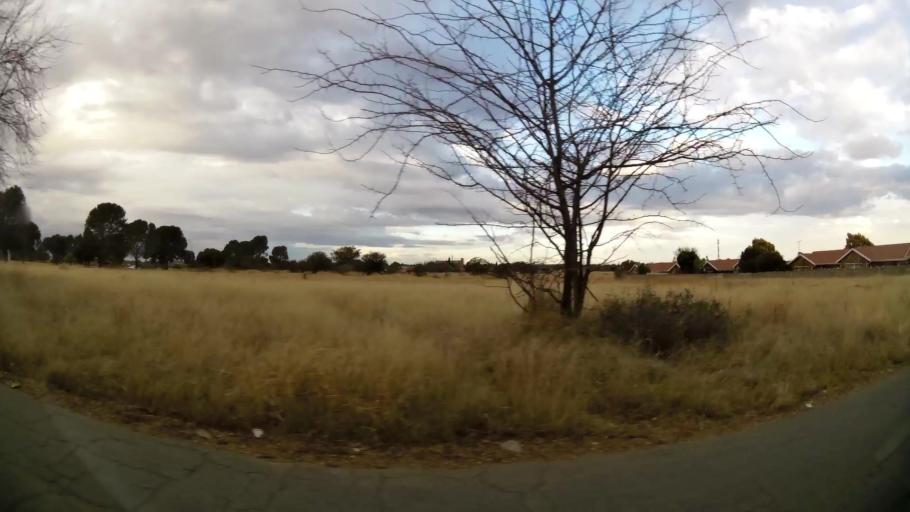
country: ZA
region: Orange Free State
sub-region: Lejweleputswa District Municipality
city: Welkom
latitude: -27.9751
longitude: 26.7002
